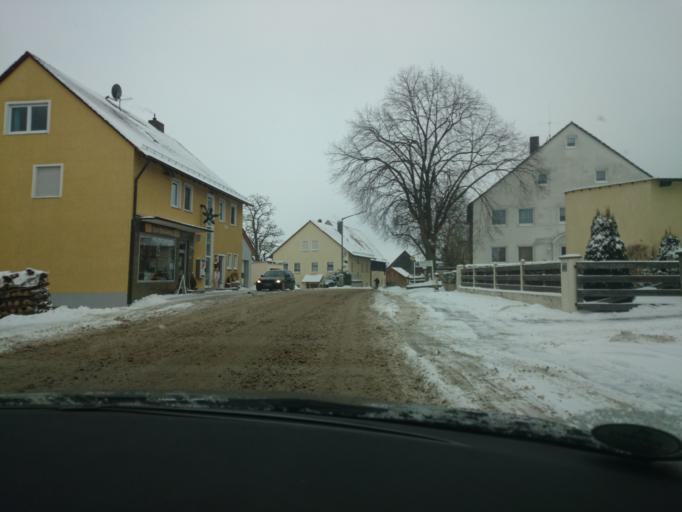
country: DE
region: Bavaria
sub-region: Regierungsbezirk Mittelfranken
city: Thalmassing
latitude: 49.1312
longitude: 11.2107
